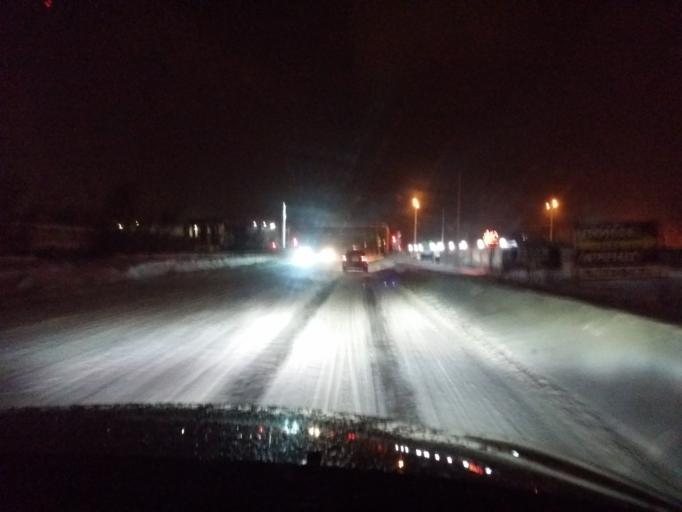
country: RU
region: Khanty-Mansiyskiy Avtonomnyy Okrug
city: Nizhnevartovsk
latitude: 60.9474
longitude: 76.5481
